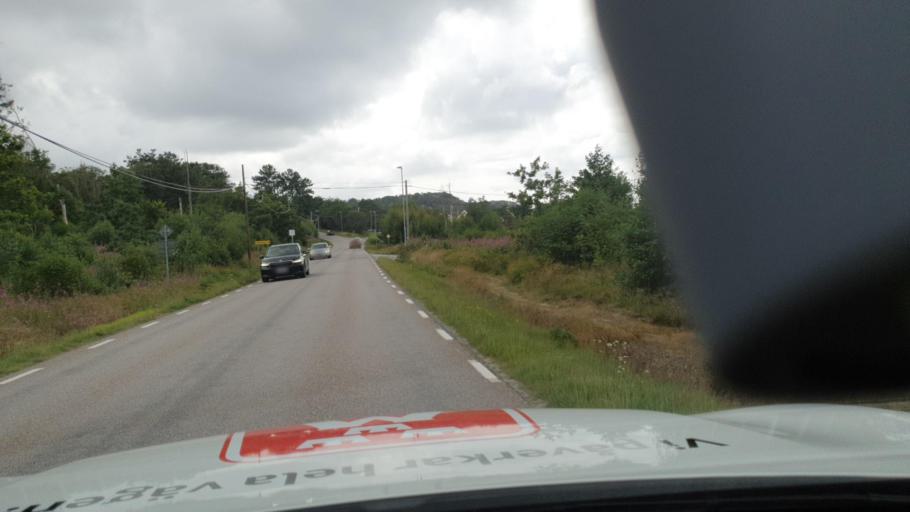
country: SE
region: Vaestra Goetaland
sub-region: Tanums Kommun
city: Grebbestad
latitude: 58.6319
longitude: 11.2804
